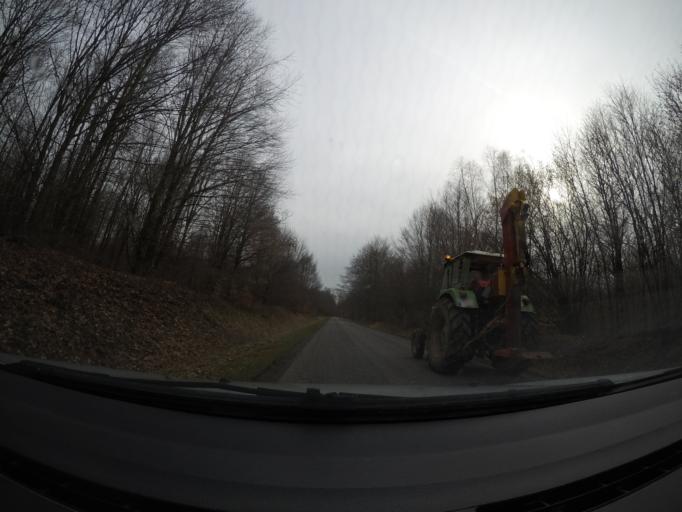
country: BE
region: Wallonia
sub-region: Province du Luxembourg
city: Martelange
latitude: 49.7850
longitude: 5.6873
